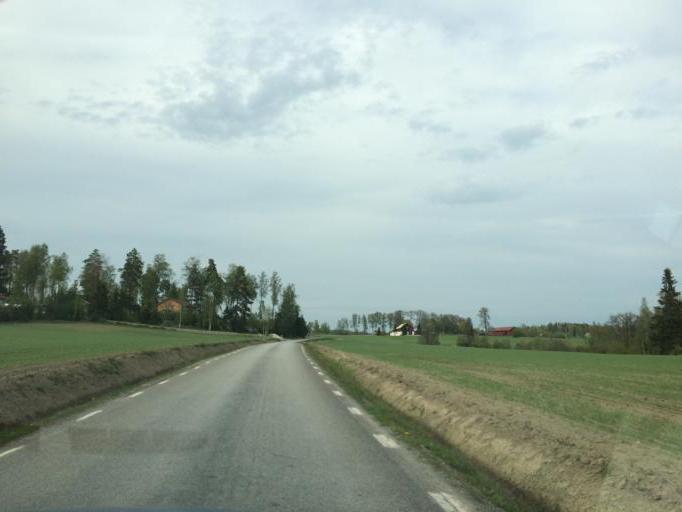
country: SE
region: Vaestmanland
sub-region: Kopings Kommun
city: Koping
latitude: 59.5918
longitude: 15.9939
